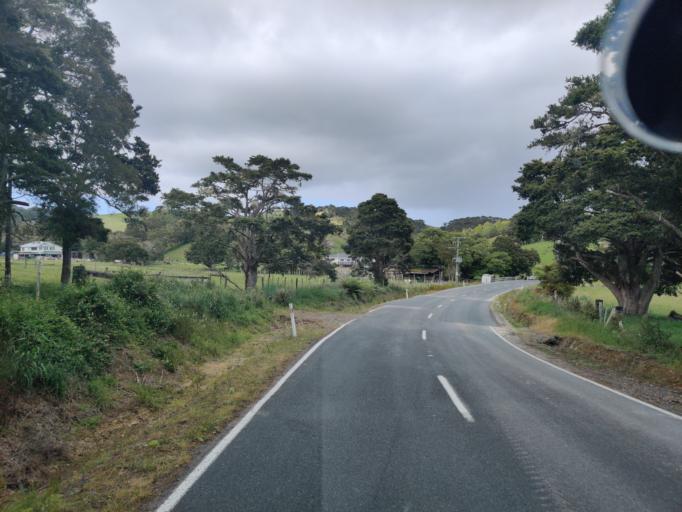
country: NZ
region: Northland
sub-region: Whangarei
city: Ngunguru
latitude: -35.5771
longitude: 174.4002
